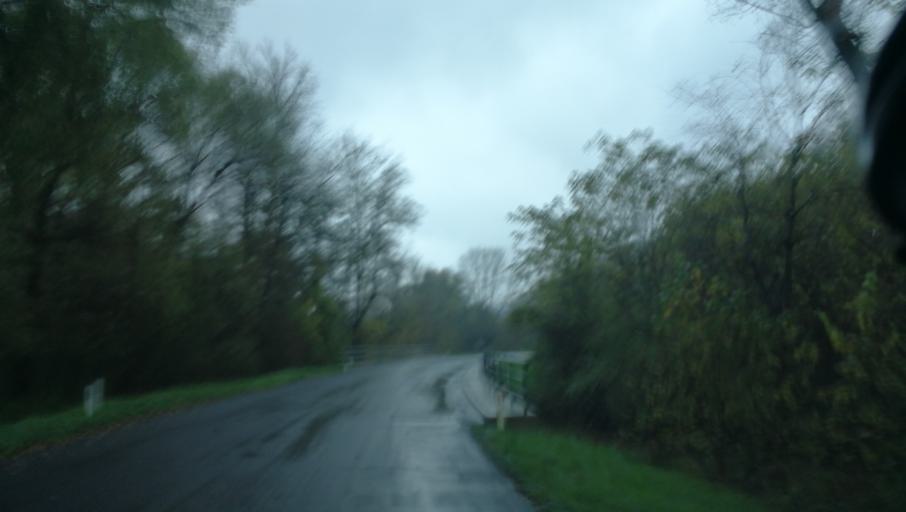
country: AT
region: Styria
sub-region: Politischer Bezirk Leibnitz
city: Strass in Steiermark
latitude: 46.7137
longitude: 15.6236
